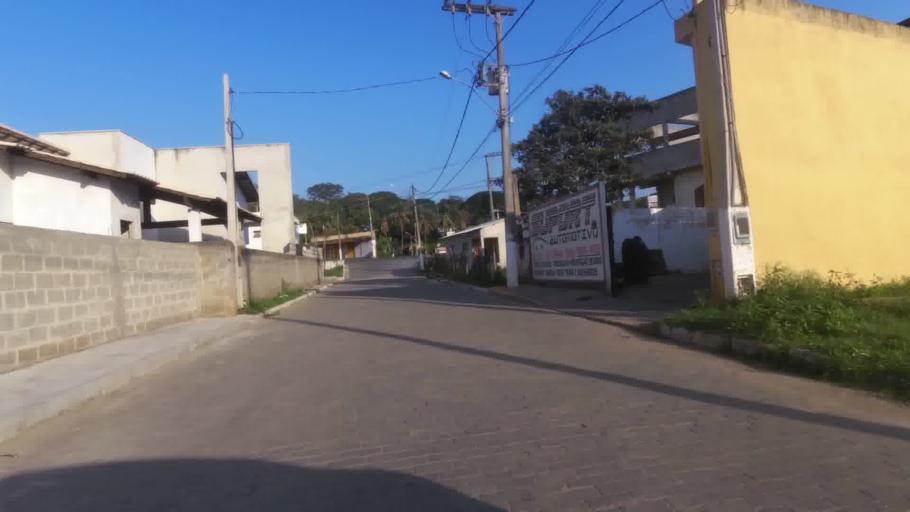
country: BR
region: Espirito Santo
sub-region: Piuma
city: Piuma
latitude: -20.8360
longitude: -40.7193
